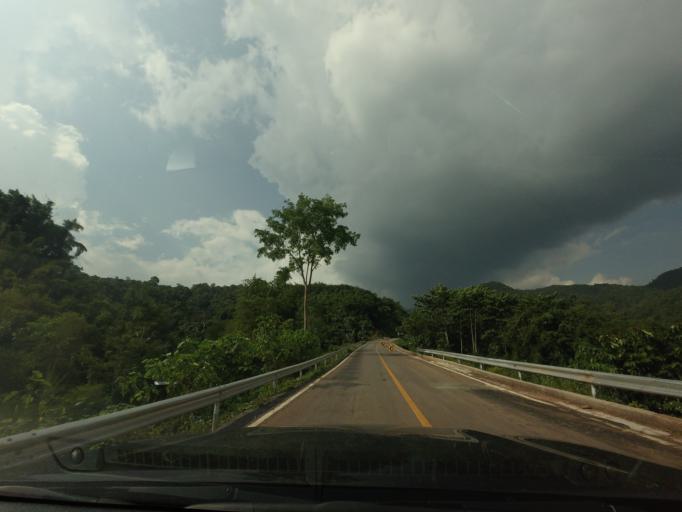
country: TH
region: Nan
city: Bo Kluea
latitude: 19.2328
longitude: 101.1822
